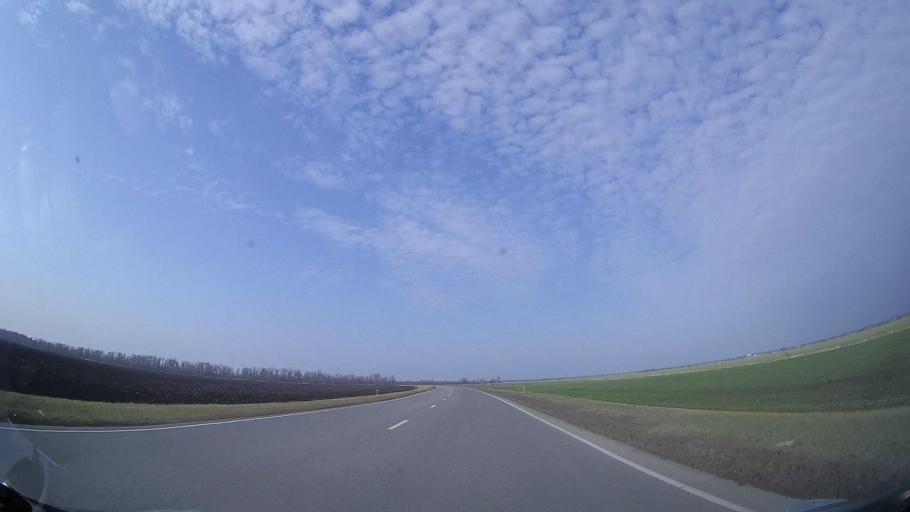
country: RU
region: Rostov
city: Tselina
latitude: 46.5138
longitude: 41.0449
